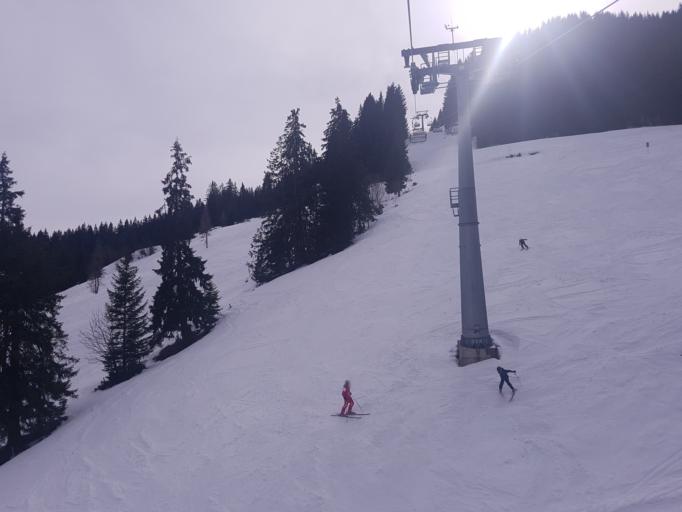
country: AT
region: Tyrol
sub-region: Politischer Bezirk Kufstein
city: Worgl
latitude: 47.4362
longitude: 12.0839
